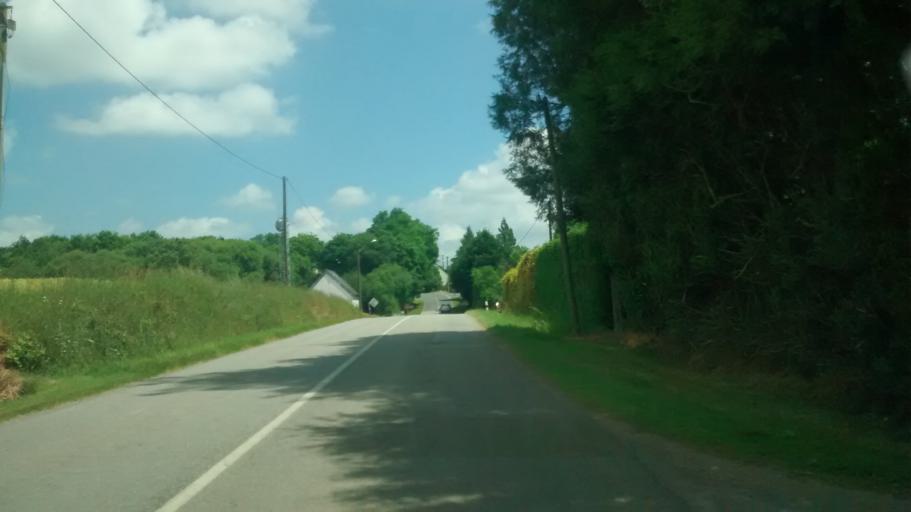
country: FR
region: Brittany
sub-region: Departement du Morbihan
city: Augan
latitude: 47.8713
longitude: -2.2160
